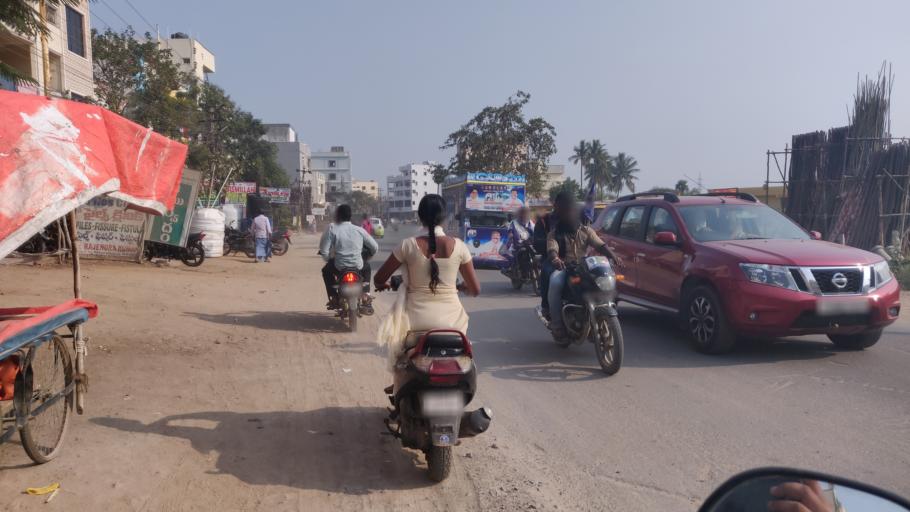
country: IN
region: Telangana
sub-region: Rangareddi
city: Uppal Kalan
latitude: 17.3931
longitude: 78.5962
